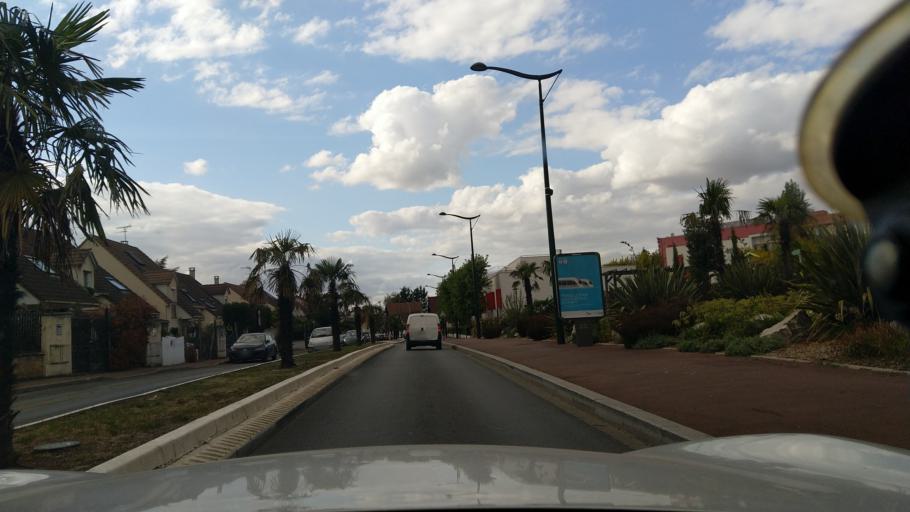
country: FR
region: Ile-de-France
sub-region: Departement de Seine-Saint-Denis
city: Bondy
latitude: 48.9193
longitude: 2.4754
